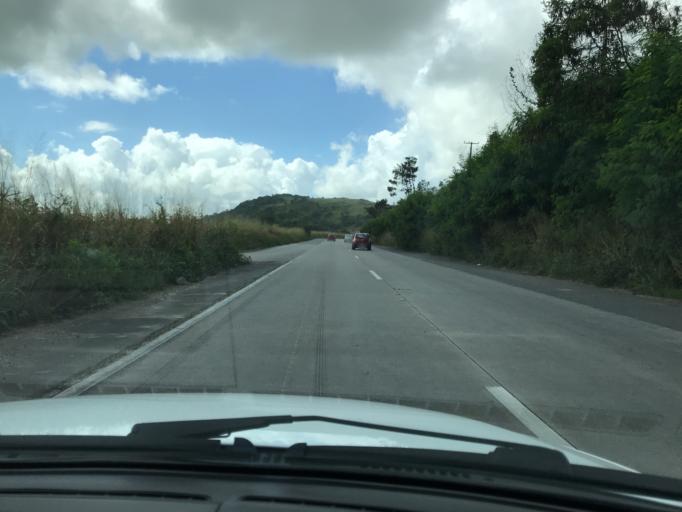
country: BR
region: Pernambuco
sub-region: Vitoria De Santo Antao
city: Vitoria de Santo Antao
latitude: -8.1144
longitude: -35.2405
